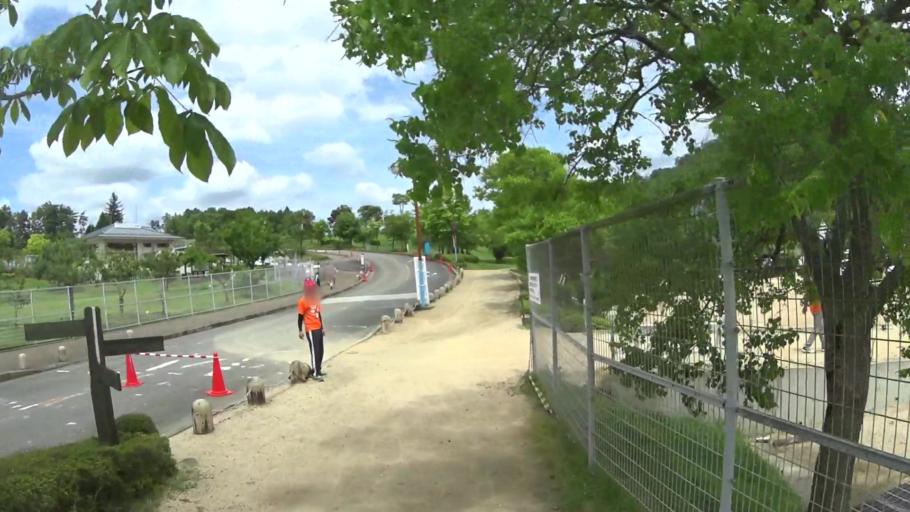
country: JP
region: Kyoto
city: Ayabe
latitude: 35.1627
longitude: 135.4157
